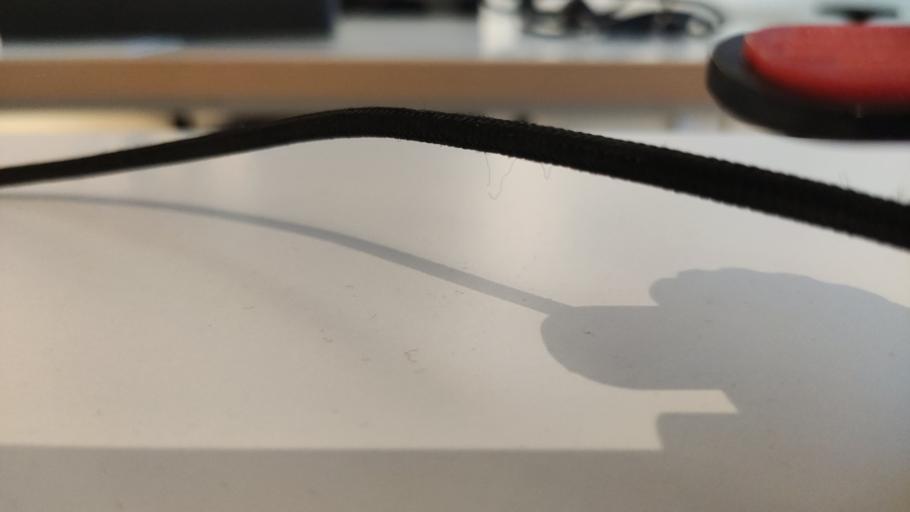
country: RU
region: Moskovskaya
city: Sychevo
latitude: 55.8176
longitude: 36.3014
